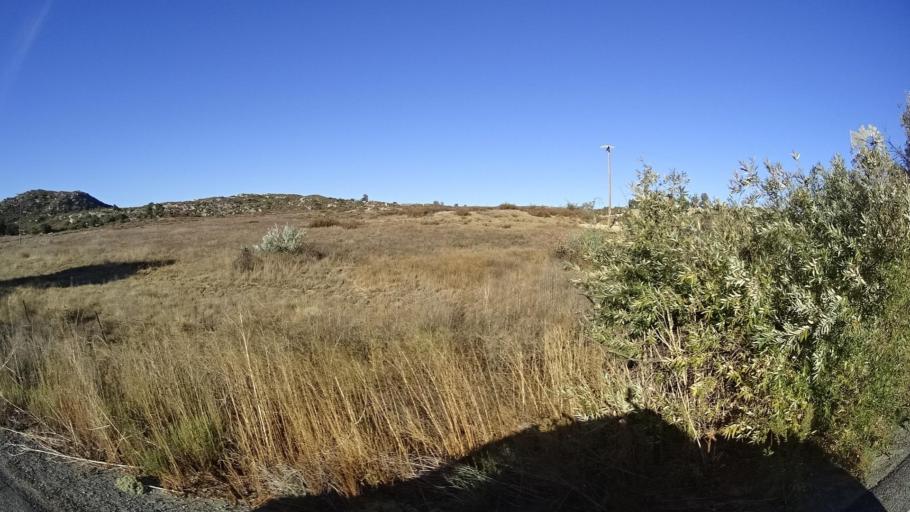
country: US
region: California
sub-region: San Diego County
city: Campo
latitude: 32.6197
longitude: -116.4757
